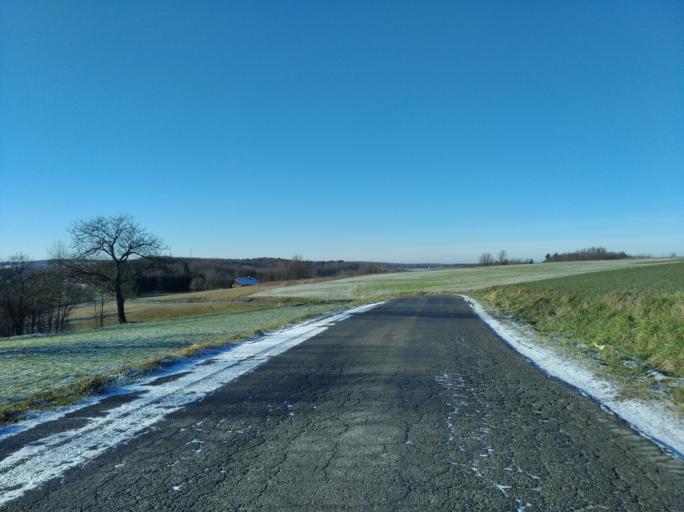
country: PL
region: Subcarpathian Voivodeship
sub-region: Powiat ropczycko-sedziszowski
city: Iwierzyce
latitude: 49.9706
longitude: 21.7547
